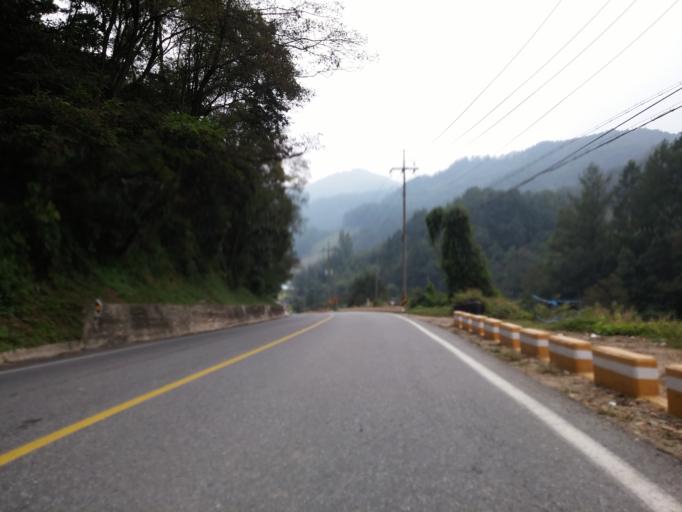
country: KR
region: Chungcheongbuk-do
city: Okcheon
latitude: 36.3967
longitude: 127.6931
